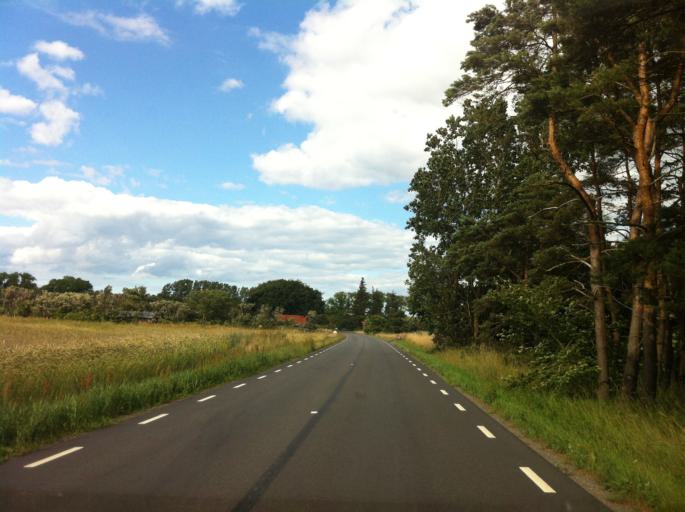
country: SE
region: Skane
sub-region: Simrishamns Kommun
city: Simrishamn
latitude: 55.4423
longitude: 14.2392
